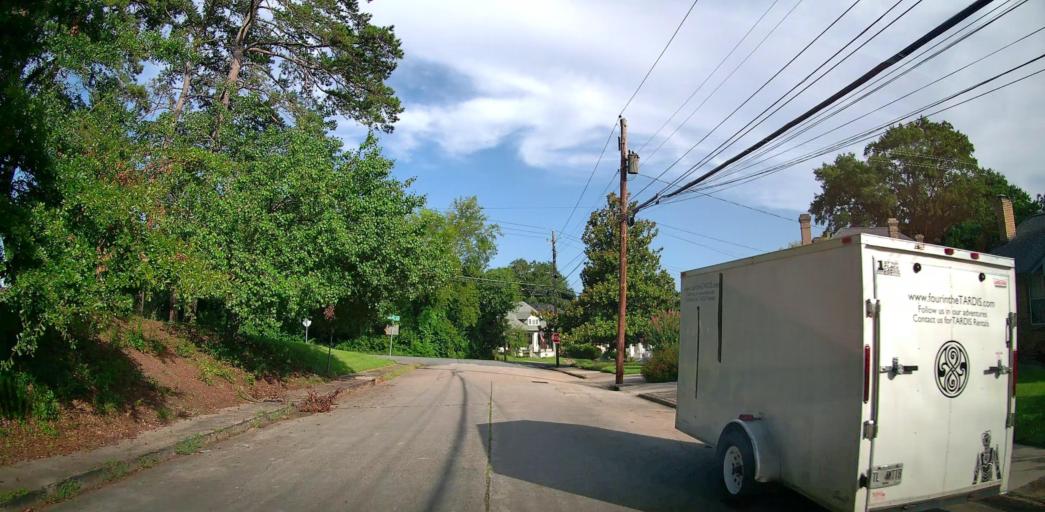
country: US
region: Georgia
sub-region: Bibb County
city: Macon
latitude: 32.8534
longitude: -83.6236
